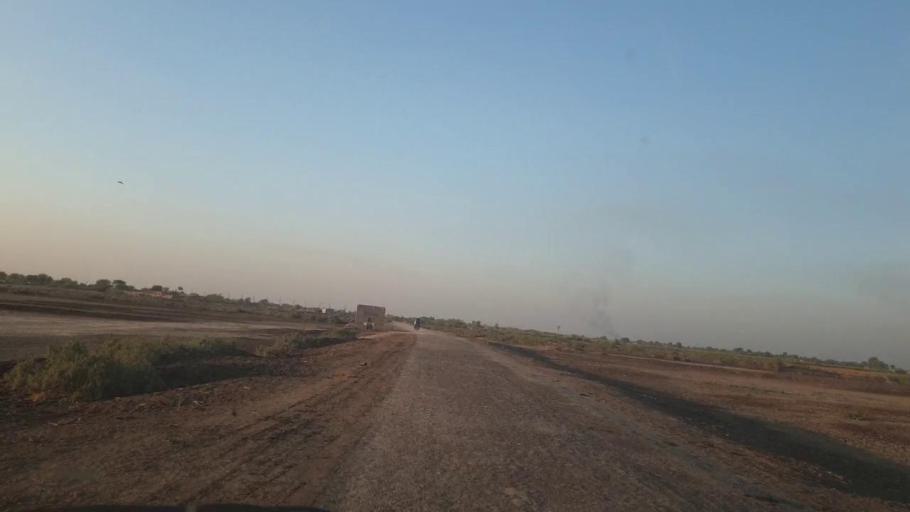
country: PK
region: Sindh
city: Mirpur Khas
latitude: 25.4609
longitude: 69.0719
